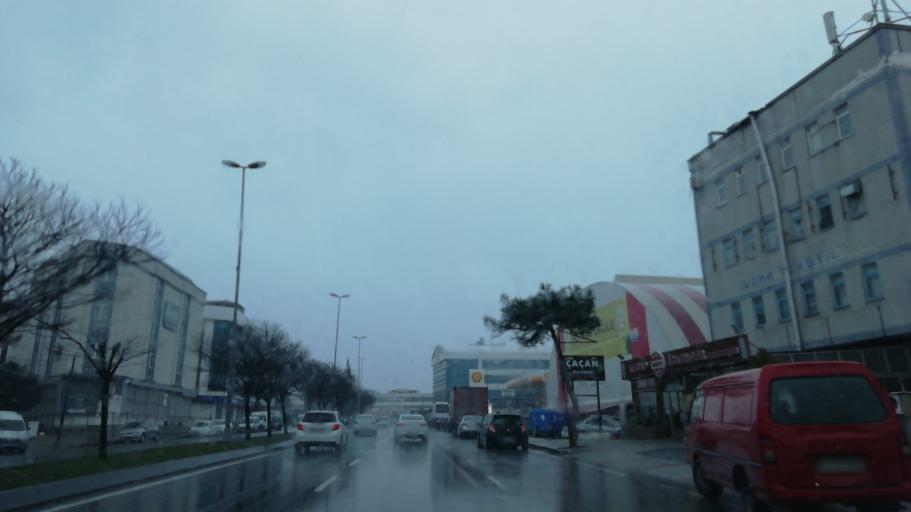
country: TR
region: Istanbul
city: Yakuplu
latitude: 40.9986
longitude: 28.7135
